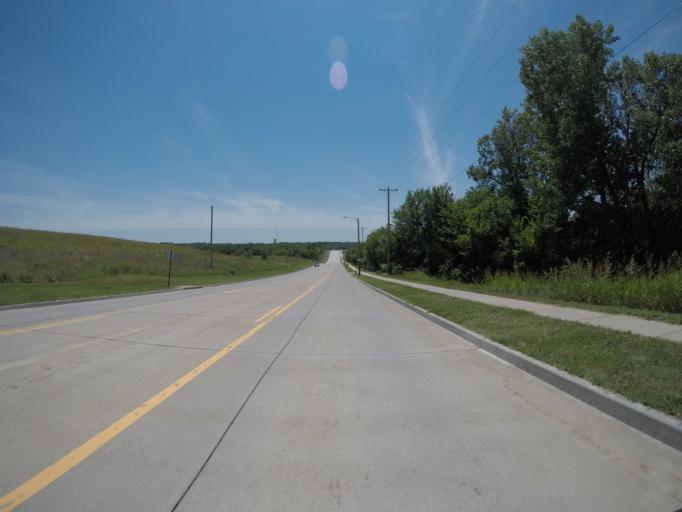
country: US
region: Kansas
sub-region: Geary County
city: Junction City
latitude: 39.0342
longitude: -96.8717
